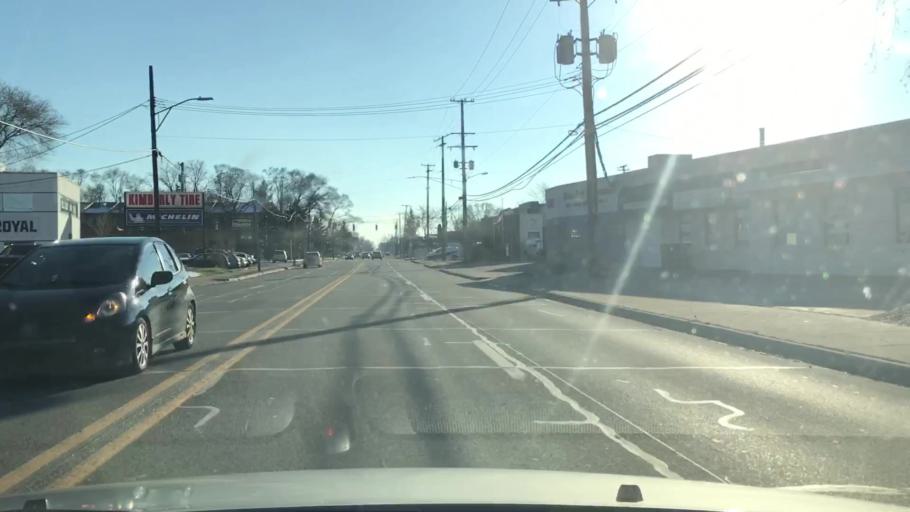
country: US
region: Michigan
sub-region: Oakland County
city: Clawson
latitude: 42.5394
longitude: -83.1345
